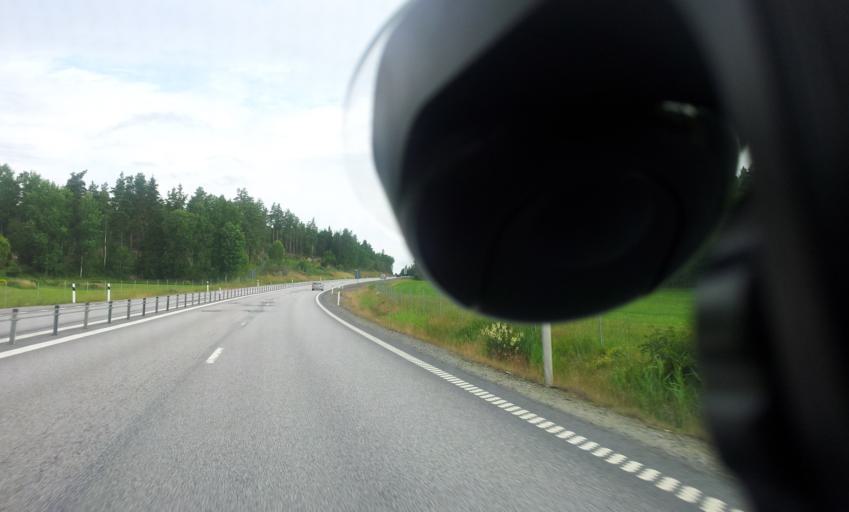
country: SE
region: OEstergoetland
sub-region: Soderkopings Kommun
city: Soederkoeping
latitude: 58.4282
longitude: 16.3845
